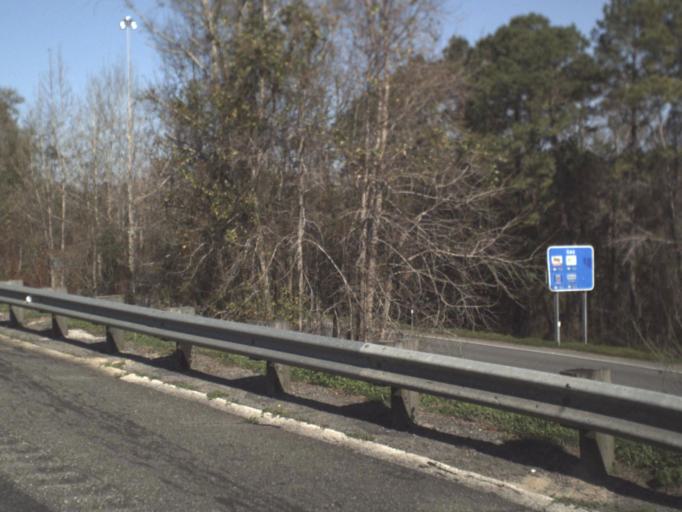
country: US
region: Florida
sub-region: Jefferson County
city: Monticello
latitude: 30.4751
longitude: -83.8867
